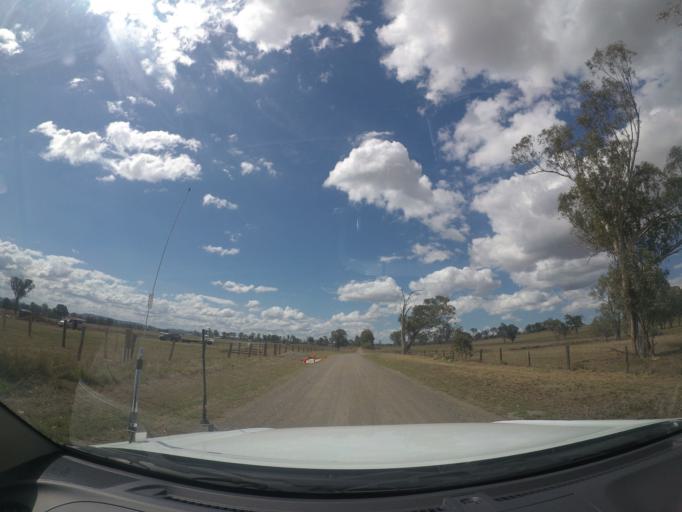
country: AU
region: Queensland
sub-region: Logan
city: Cedar Vale
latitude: -27.8933
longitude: 152.9590
